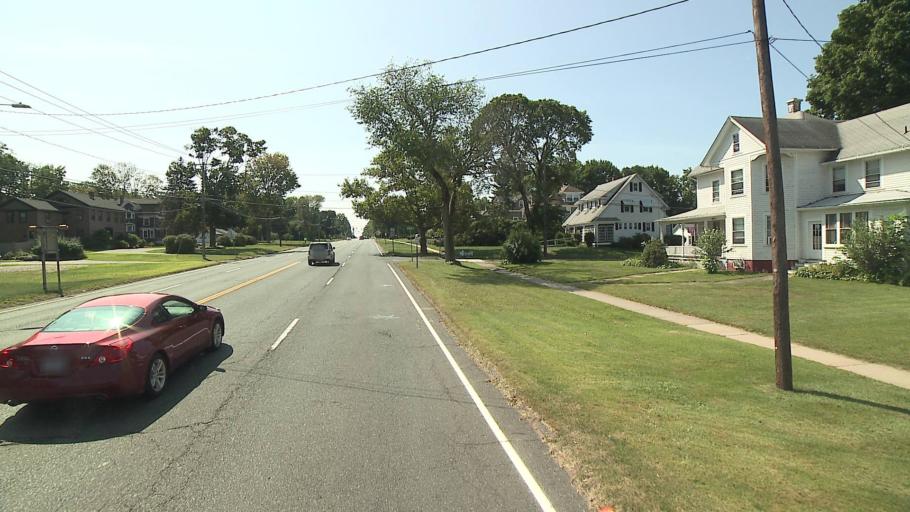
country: US
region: Connecticut
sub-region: Hartford County
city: Thompsonville
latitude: 41.9934
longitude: -72.5942
